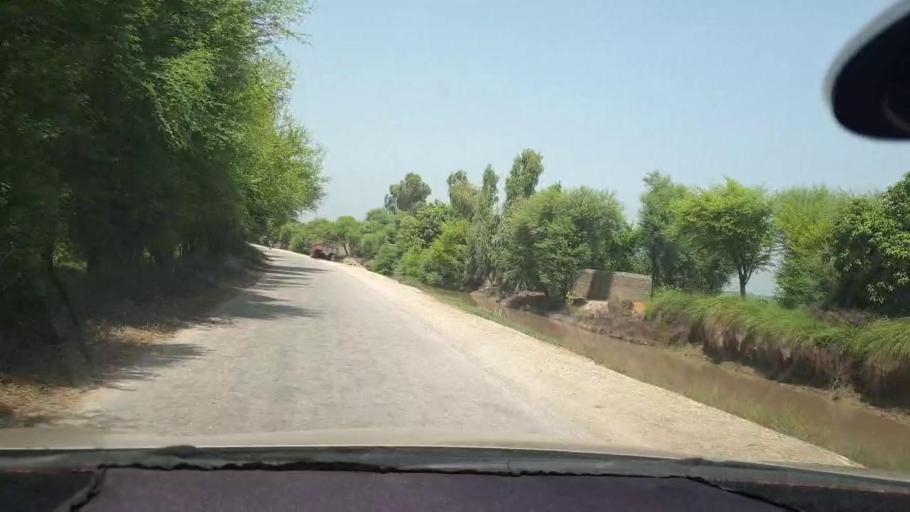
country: PK
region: Sindh
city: Kambar
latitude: 27.6480
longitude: 67.9689
